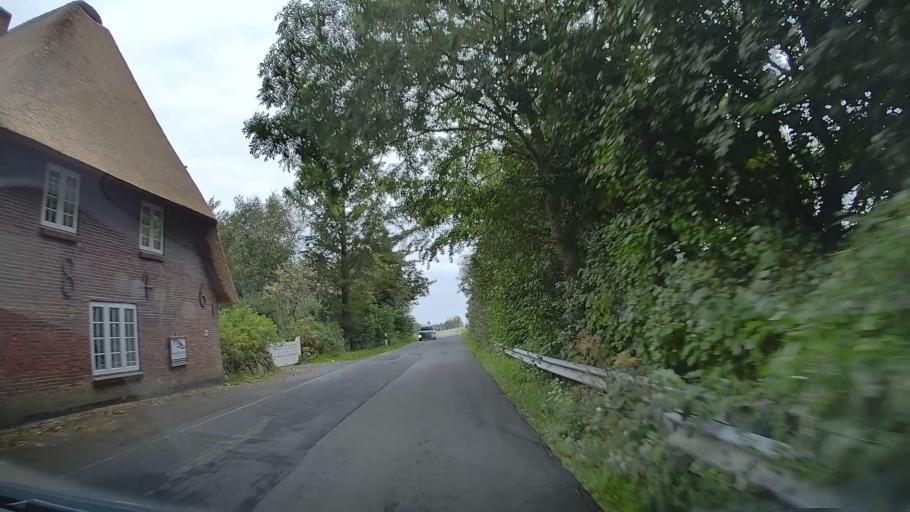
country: DE
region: Schleswig-Holstein
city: Galmsbull
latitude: 54.7859
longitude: 8.7326
